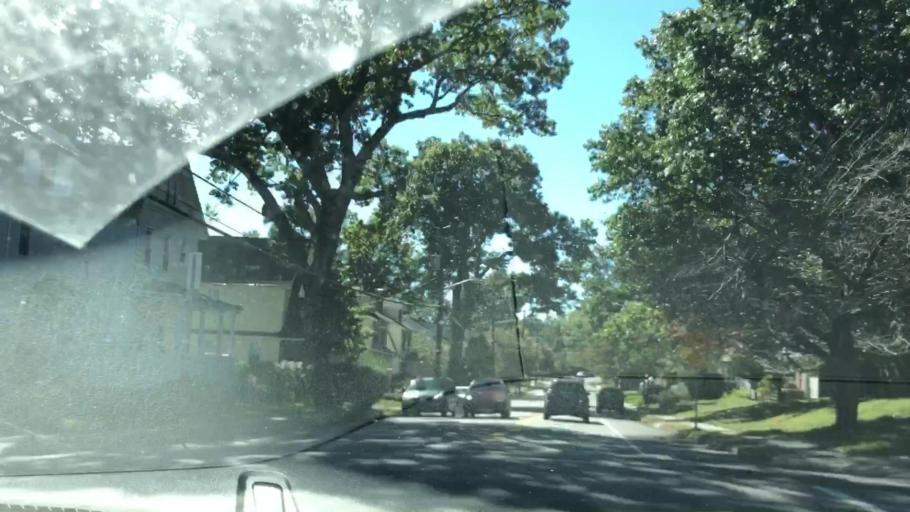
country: US
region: New Jersey
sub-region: Essex County
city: West Orange
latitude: 40.7986
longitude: -74.2265
